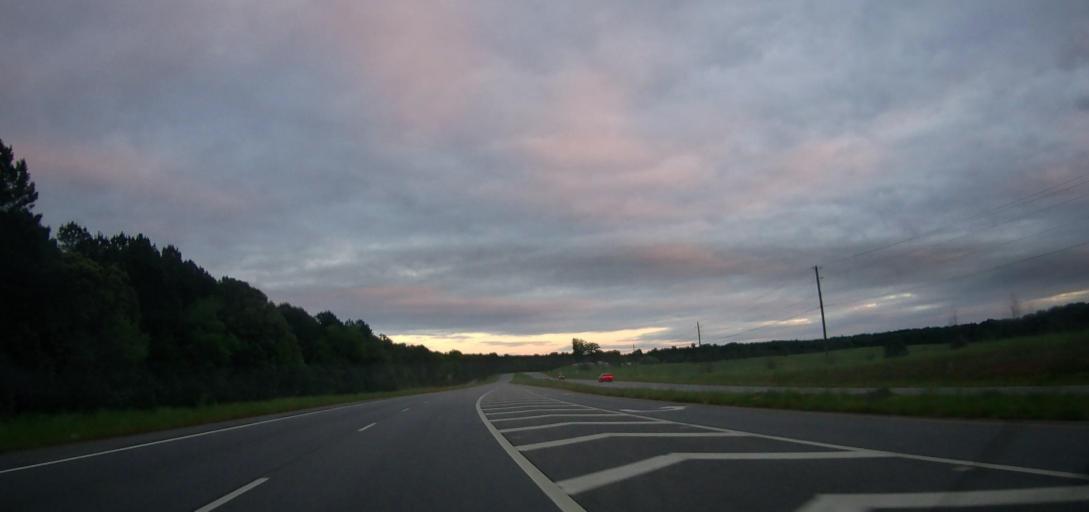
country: US
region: Georgia
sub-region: Jackson County
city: Arcade
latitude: 34.0329
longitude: -83.4978
